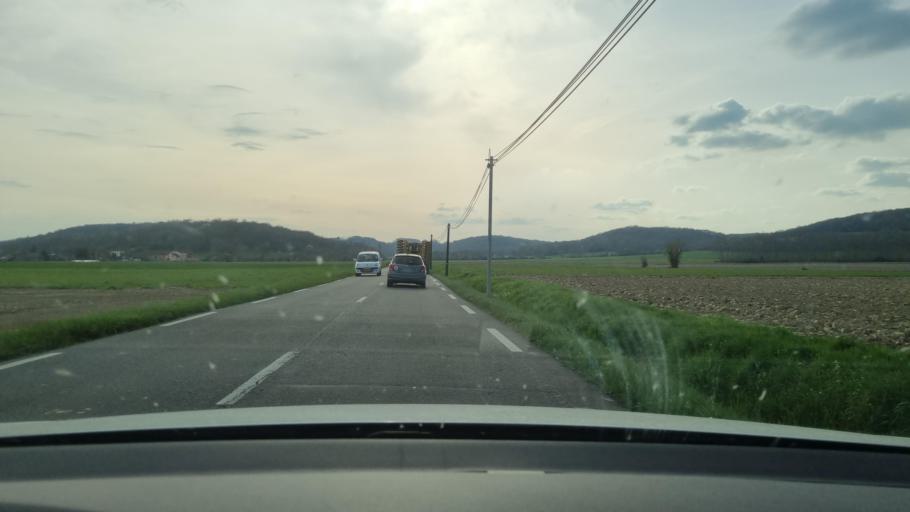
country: FR
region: Midi-Pyrenees
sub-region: Departement des Hautes-Pyrenees
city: Vic-en-Bigorre
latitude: 43.3894
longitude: 0.0138
